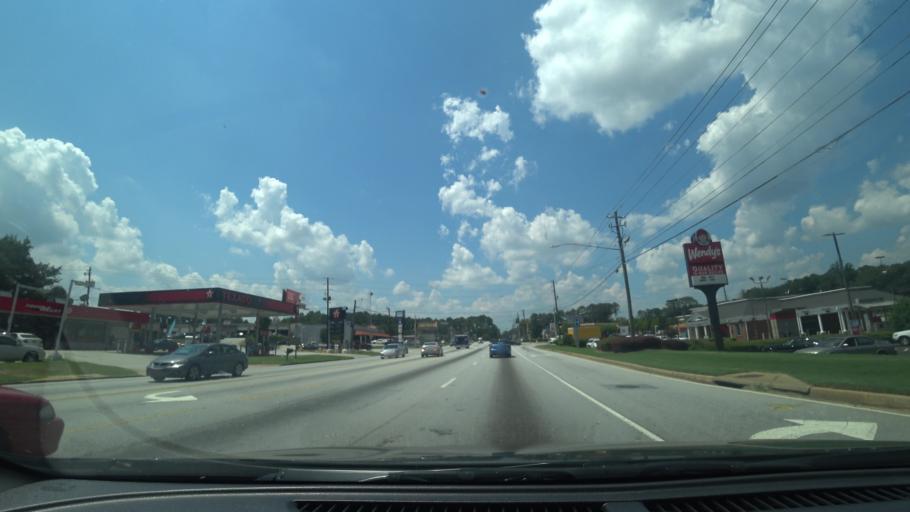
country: US
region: Georgia
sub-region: DeKalb County
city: Redan
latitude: 33.7224
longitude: -84.1659
